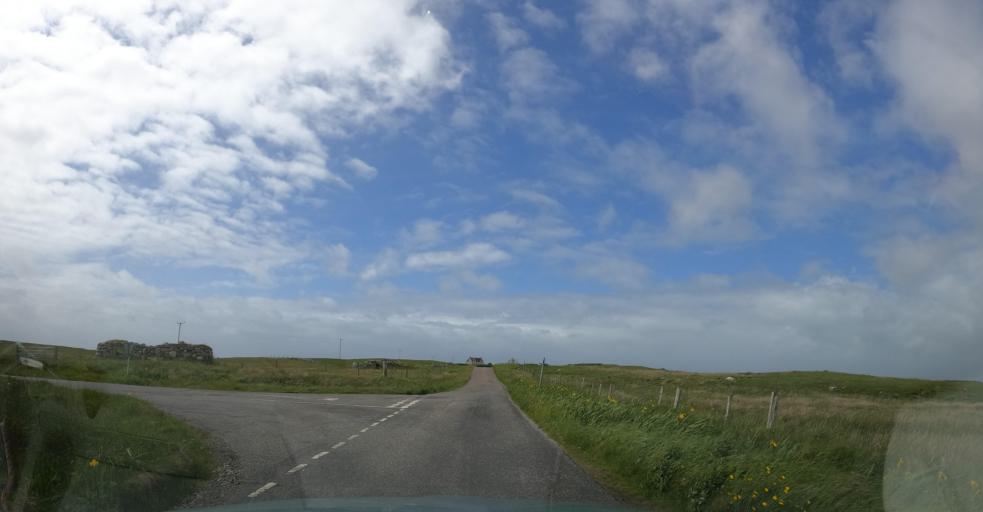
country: GB
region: Scotland
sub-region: Eilean Siar
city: Isle of South Uist
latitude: 57.2718
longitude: -7.3989
